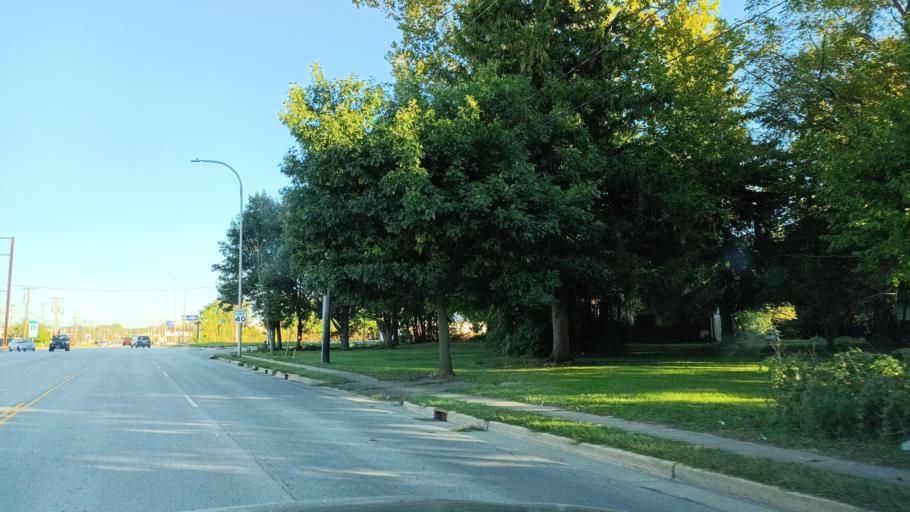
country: US
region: Illinois
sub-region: Champaign County
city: Champaign
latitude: 40.1346
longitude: -88.2635
